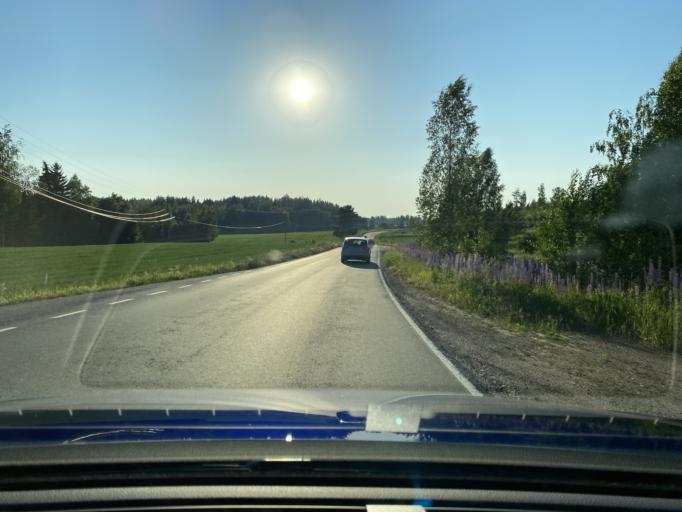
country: FI
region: Haeme
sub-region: Riihimaeki
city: Riihimaeki
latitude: 60.7288
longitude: 24.6785
